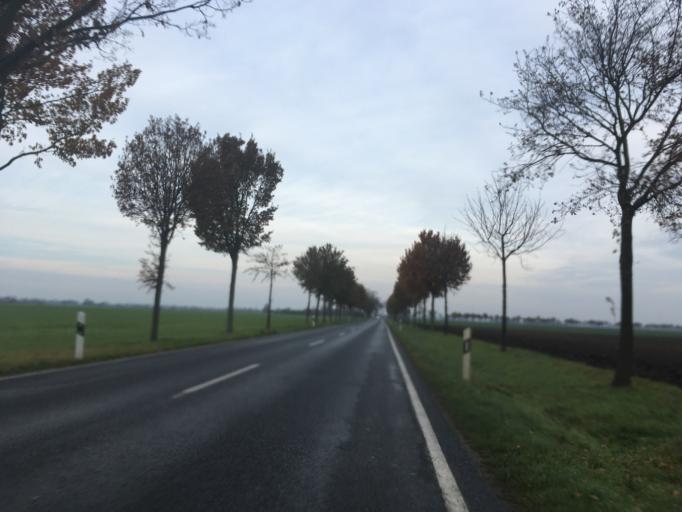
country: DE
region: Brandenburg
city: Letschin
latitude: 52.6031
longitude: 14.3483
